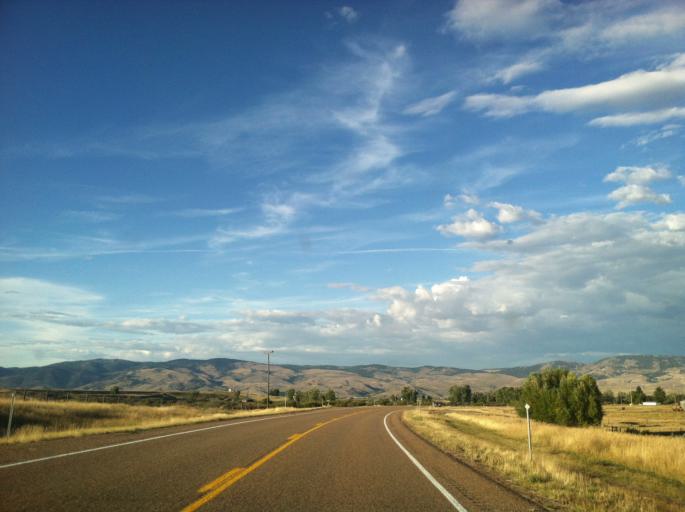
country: US
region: Montana
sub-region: Granite County
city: Philipsburg
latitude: 46.6071
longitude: -113.1848
